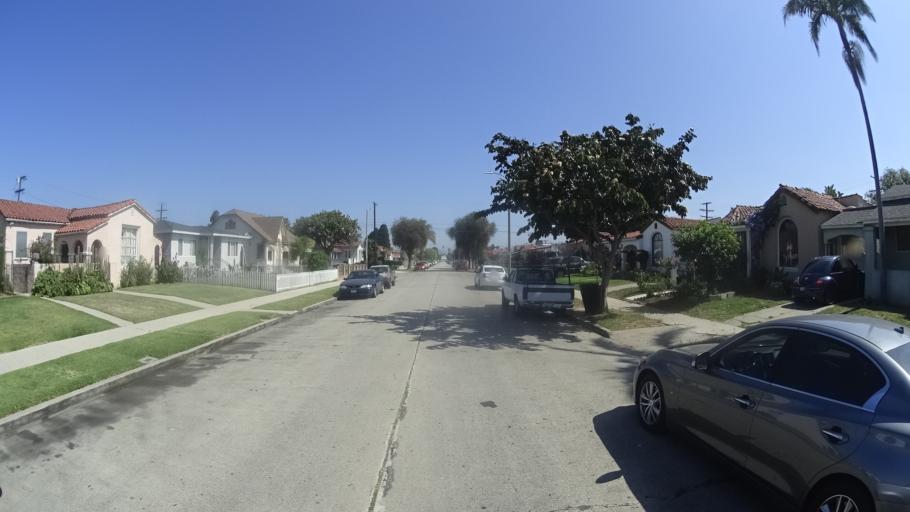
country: US
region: California
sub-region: Los Angeles County
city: View Park-Windsor Hills
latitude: 33.9795
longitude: -118.3168
